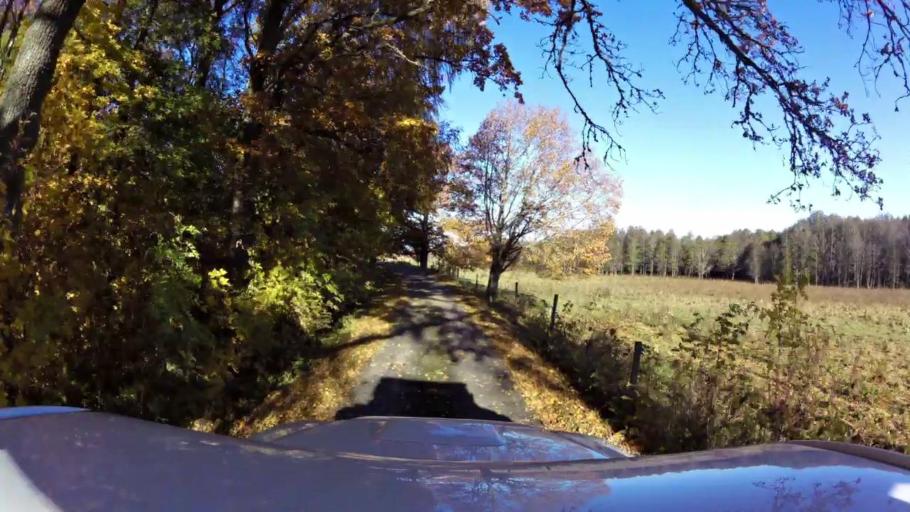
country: SE
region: OEstergoetland
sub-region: Linkopings Kommun
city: Ljungsbro
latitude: 58.5365
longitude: 15.3998
